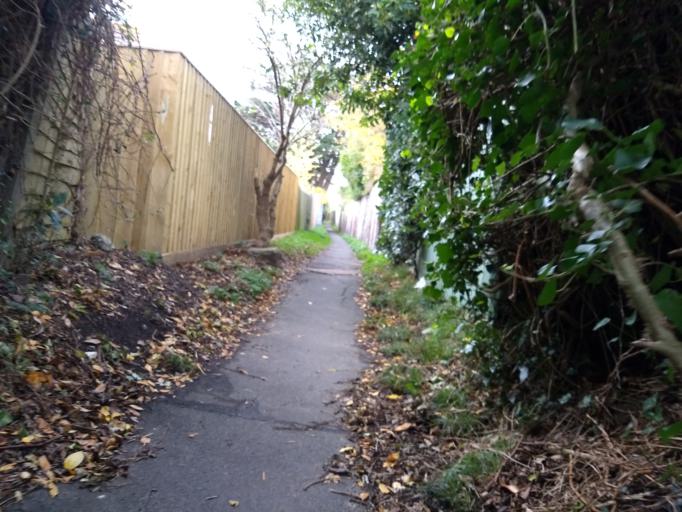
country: GB
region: England
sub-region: Isle of Wight
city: Freshwater
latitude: 50.6842
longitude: -1.5129
